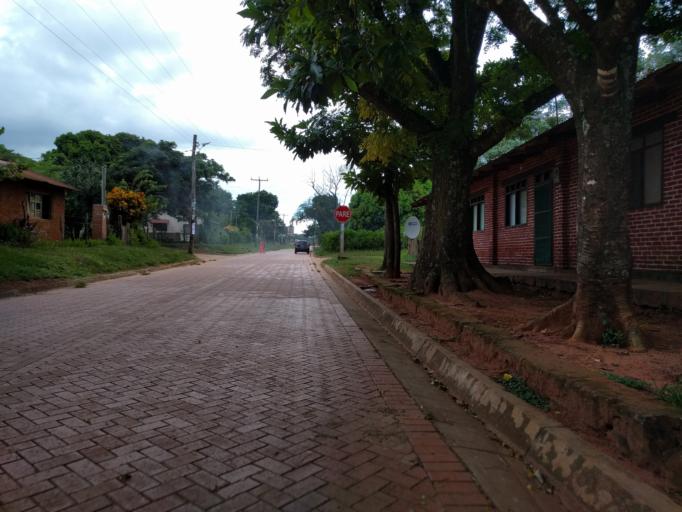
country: BO
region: Santa Cruz
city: Robore
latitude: -18.3416
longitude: -59.6011
